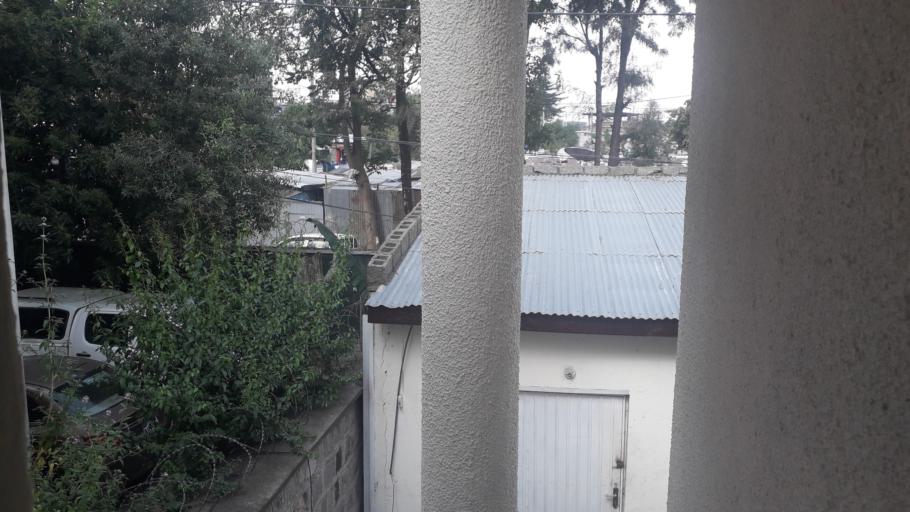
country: ET
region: Adis Abeba
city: Addis Ababa
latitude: 9.0089
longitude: 38.7931
